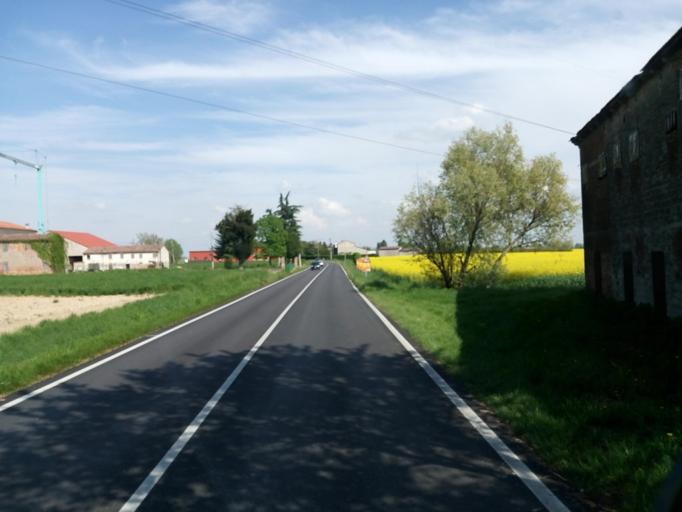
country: IT
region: Veneto
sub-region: Provincia di Verona
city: Cerea
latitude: 45.2003
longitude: 11.2287
